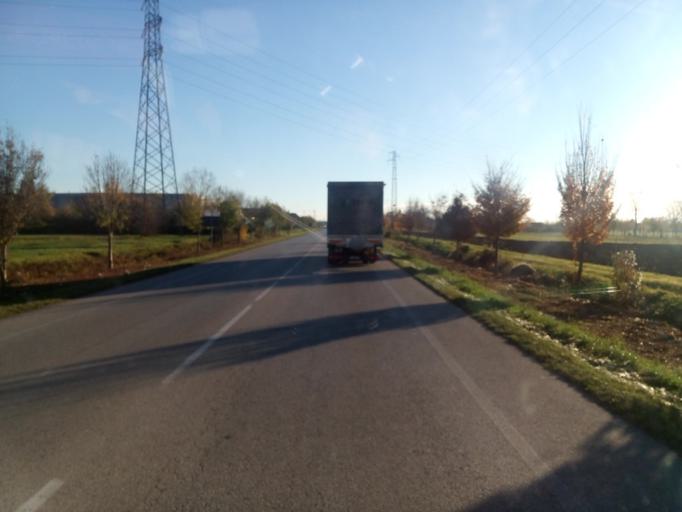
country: IT
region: Veneto
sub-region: Provincia di Vicenza
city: Sarcedo
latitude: 45.6928
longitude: 11.5232
